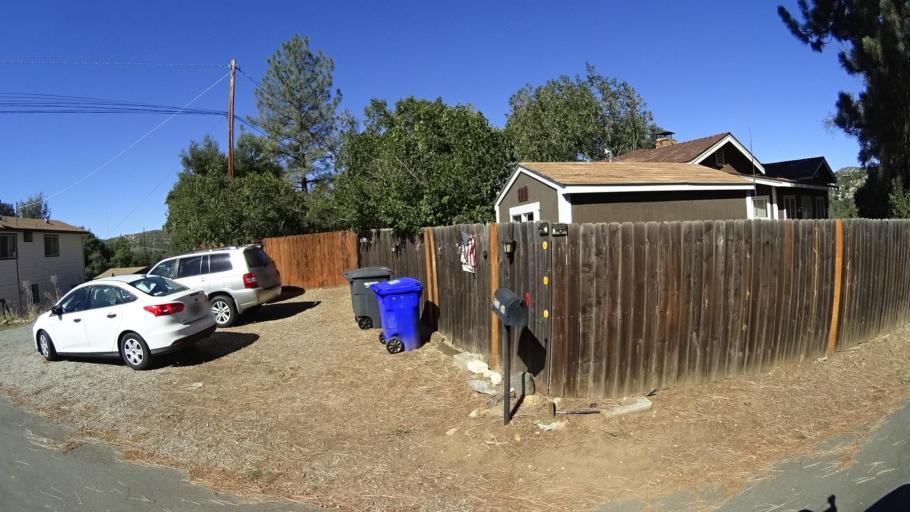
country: US
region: California
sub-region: San Diego County
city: Descanso
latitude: 32.8563
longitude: -116.6040
